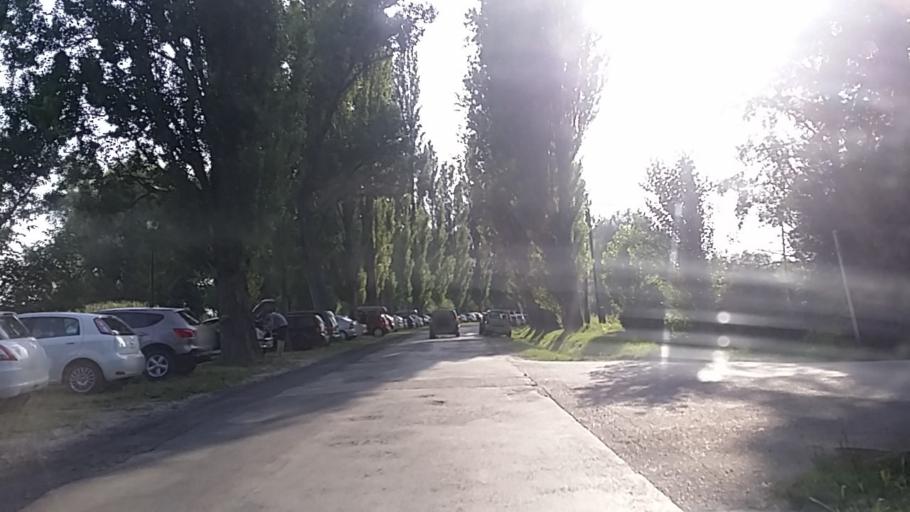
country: HU
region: Veszprem
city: Badacsonytomaj
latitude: 46.7859
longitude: 17.4419
